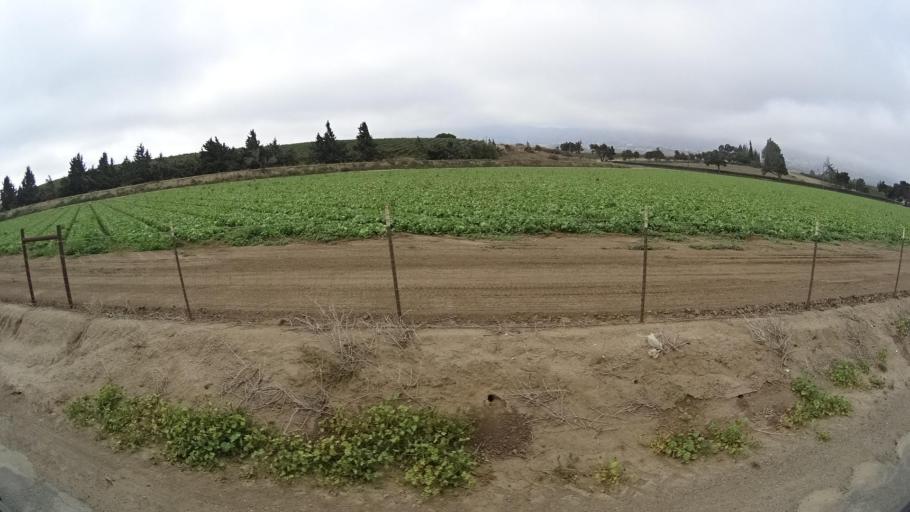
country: US
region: California
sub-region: Monterey County
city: Soledad
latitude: 36.3748
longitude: -121.3234
